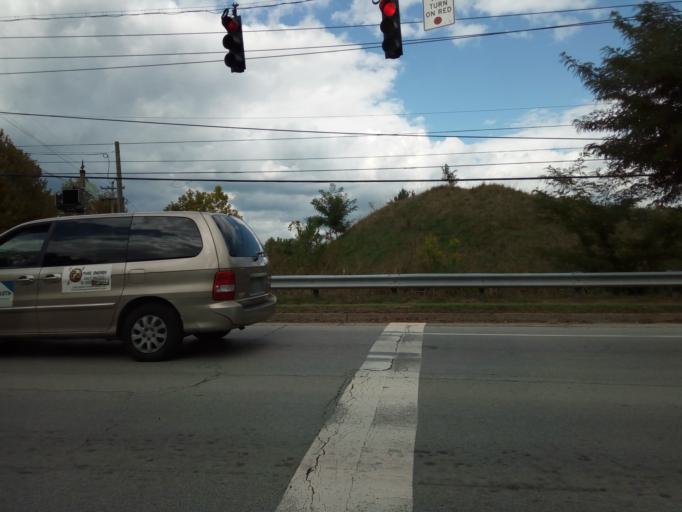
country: US
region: Kentucky
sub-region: Jefferson County
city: Audubon Park
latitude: 38.2102
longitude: -85.7169
